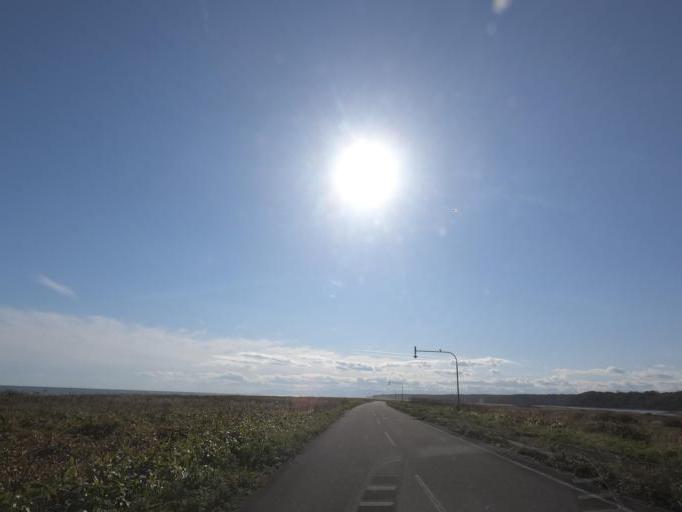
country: JP
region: Hokkaido
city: Obihiro
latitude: 42.5975
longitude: 143.5473
